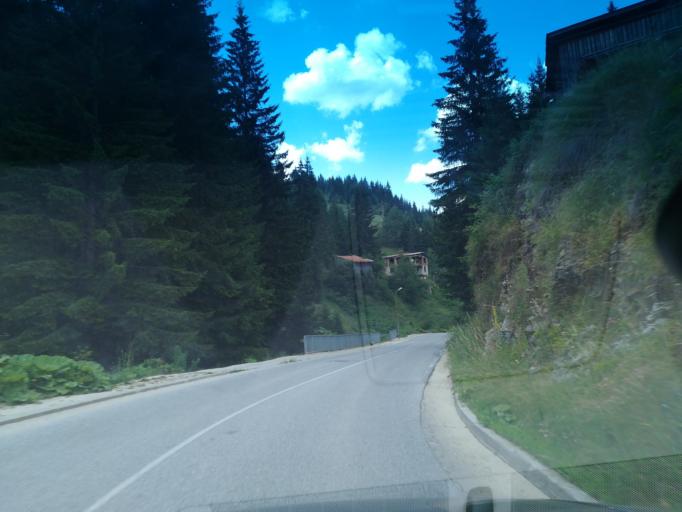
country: BG
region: Smolyan
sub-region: Obshtina Chepelare
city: Chepelare
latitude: 41.6570
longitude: 24.6328
